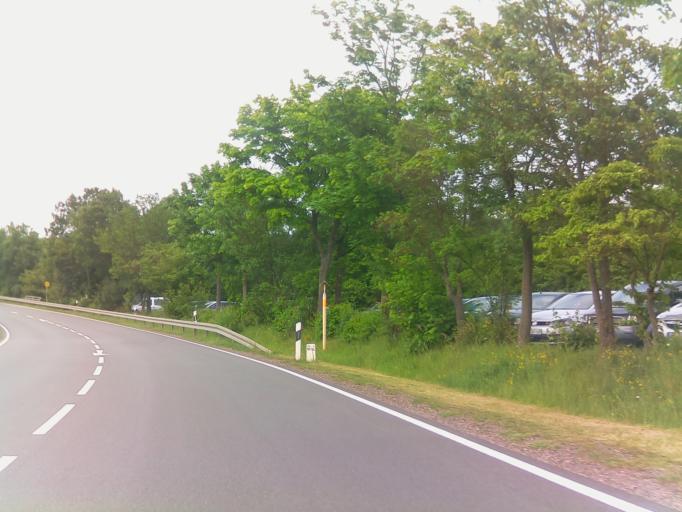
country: DE
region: Hesse
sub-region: Regierungsbezirk Kassel
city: Bad Arolsen
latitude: 51.3725
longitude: 9.0552
